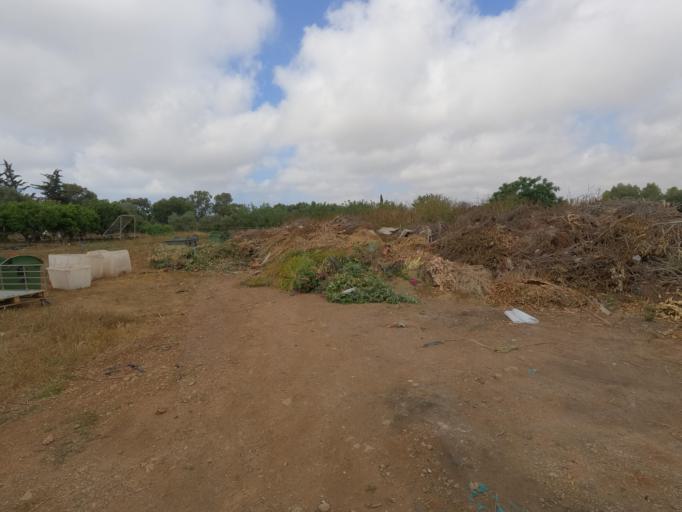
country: CY
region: Ammochostos
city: Ayia Napa
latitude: 35.0137
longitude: 34.0203
